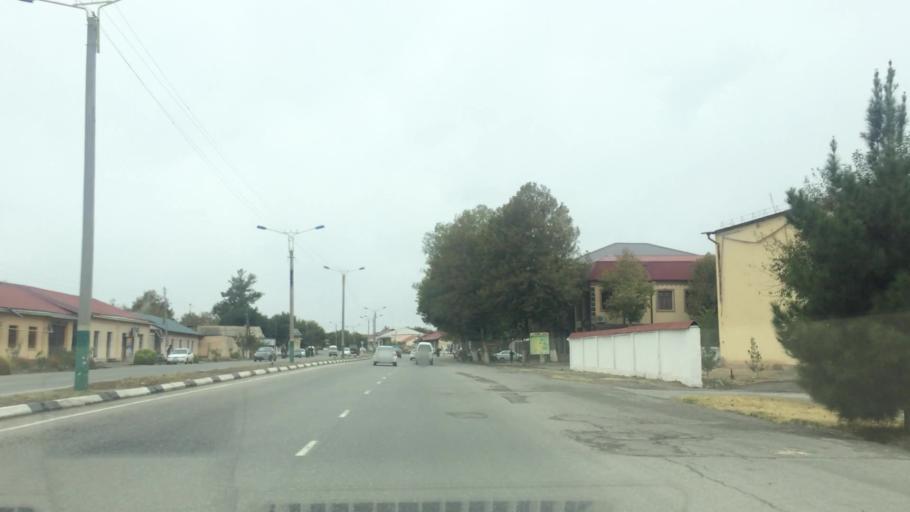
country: UZ
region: Samarqand
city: Bulung'ur
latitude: 39.7696
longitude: 67.2665
